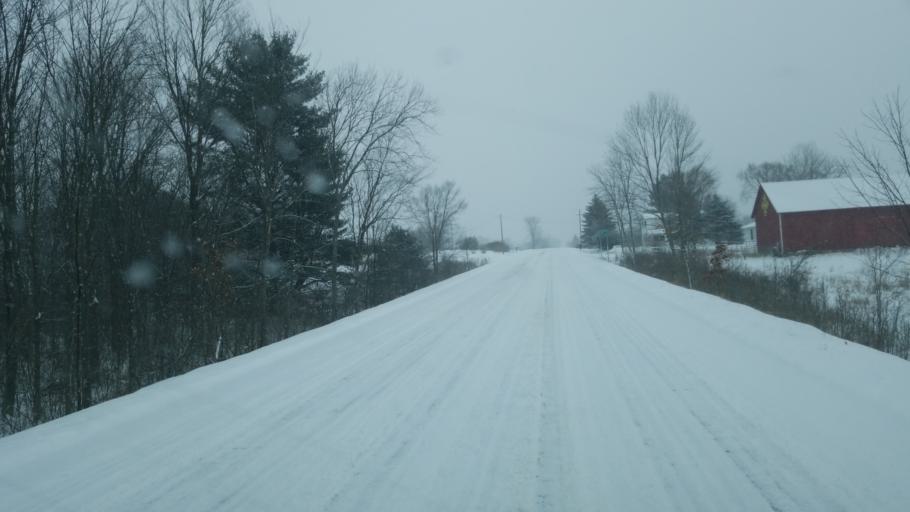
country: US
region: Michigan
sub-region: Mecosta County
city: Canadian Lakes
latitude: 43.5768
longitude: -85.4262
